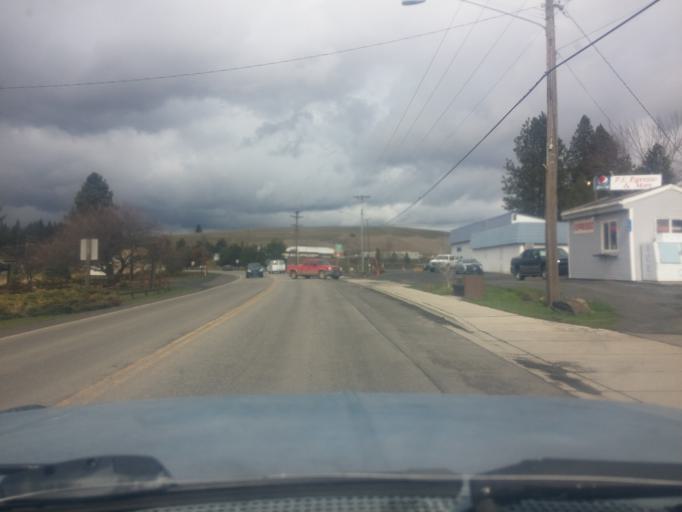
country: US
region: Idaho
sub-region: Latah County
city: Moscow
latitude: 46.9241
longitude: -116.9024
